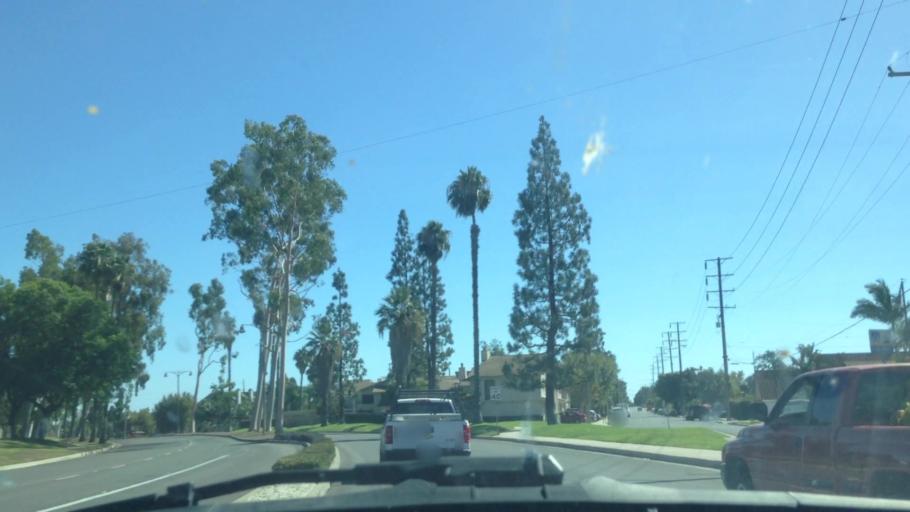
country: US
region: California
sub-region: Orange County
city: Placentia
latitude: 33.8800
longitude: -117.8636
